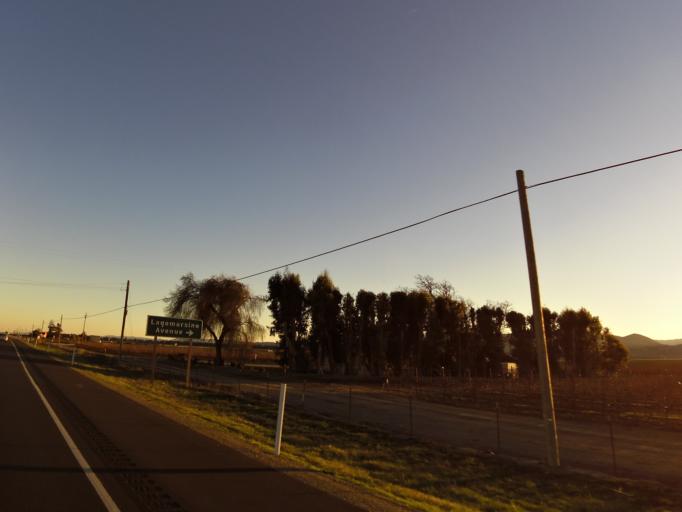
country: US
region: California
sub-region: Monterey County
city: Greenfield
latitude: 36.2896
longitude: -121.1967
